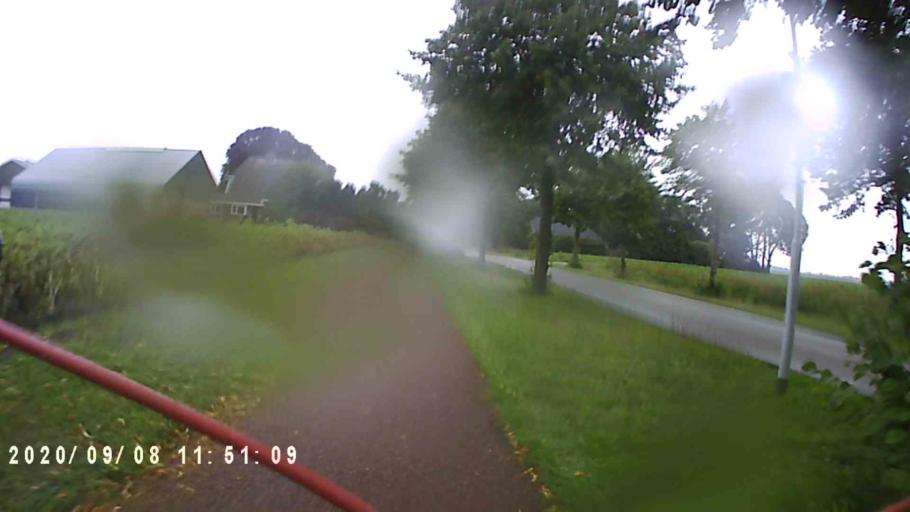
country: NL
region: Groningen
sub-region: Gemeente Hoogezand-Sappemeer
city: Sappemeer
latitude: 53.1293
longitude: 6.8102
